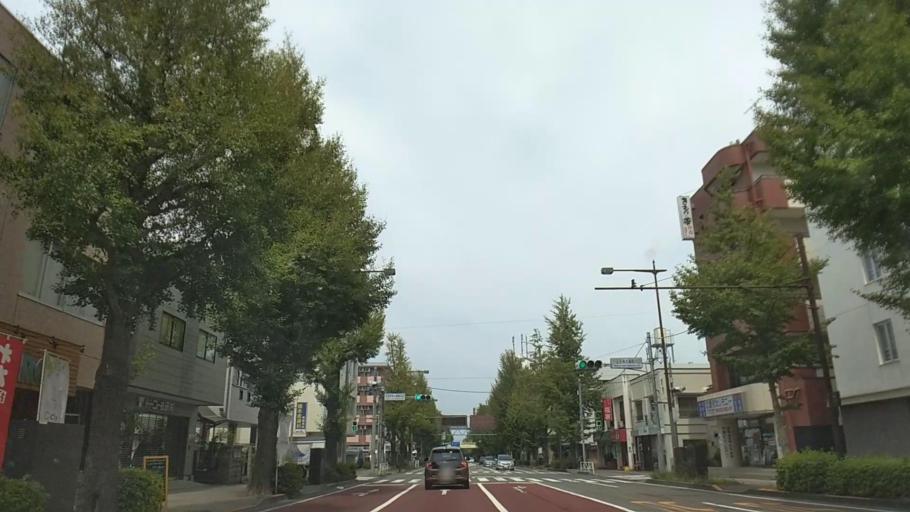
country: JP
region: Tokyo
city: Hachioji
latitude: 35.6561
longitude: 139.3087
